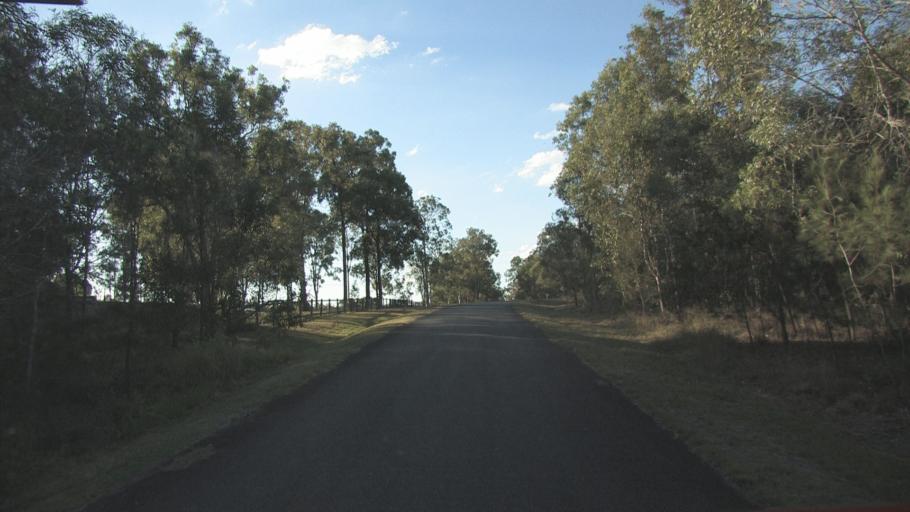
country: AU
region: Queensland
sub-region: Ipswich
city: Springfield Lakes
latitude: -27.6953
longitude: 152.9373
